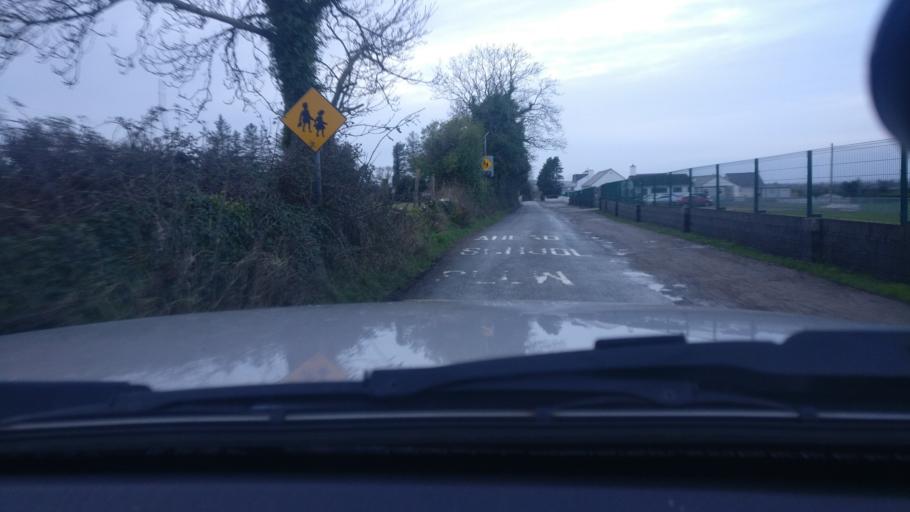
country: IE
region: Connaught
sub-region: County Galway
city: Loughrea
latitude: 53.1636
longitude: -8.5613
